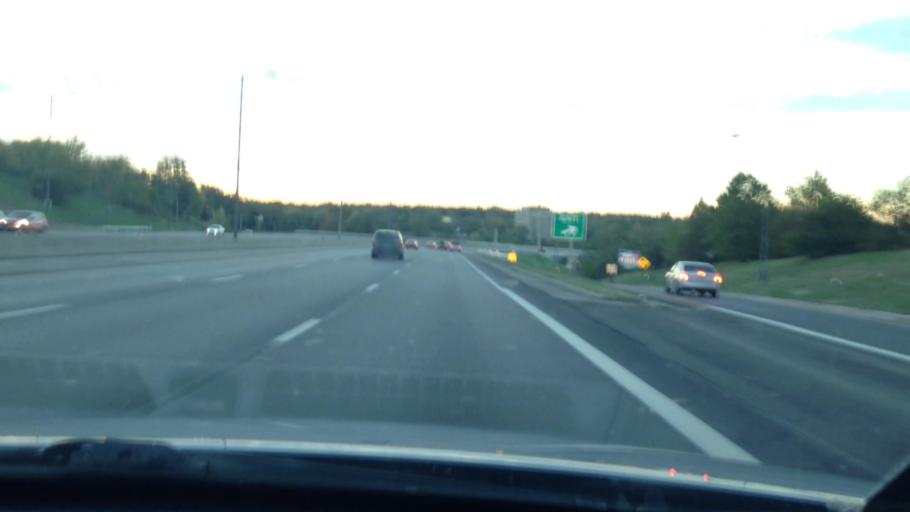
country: US
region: Kansas
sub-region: Johnson County
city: Westwood
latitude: 39.0380
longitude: -94.5559
